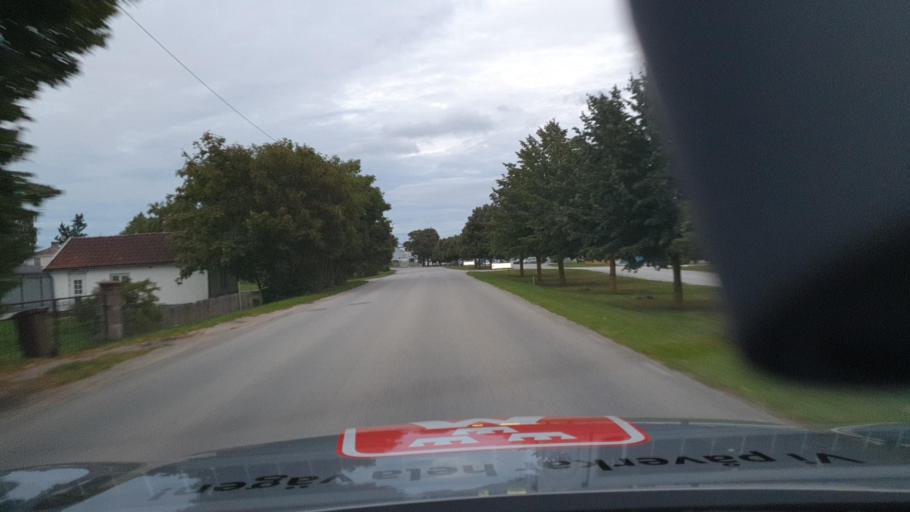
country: SE
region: Gotland
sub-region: Gotland
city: Visby
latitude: 57.6324
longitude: 18.3422
